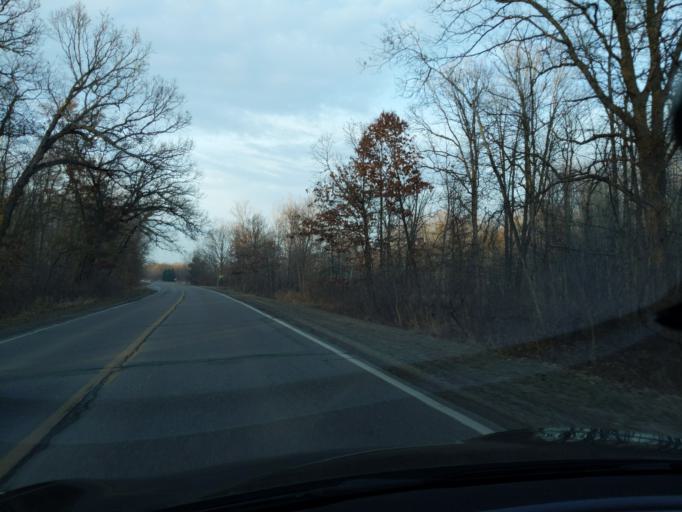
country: US
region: Michigan
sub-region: Livingston County
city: Brighton
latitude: 42.6052
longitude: -83.7486
